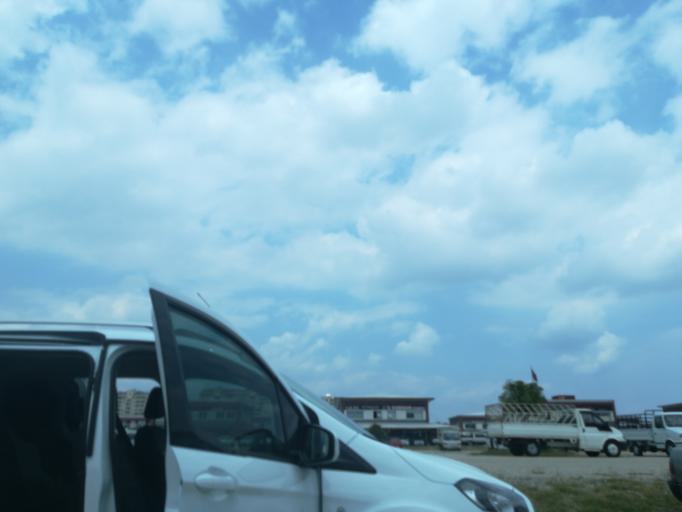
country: TR
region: Adana
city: Seyhan
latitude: 37.0003
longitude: 35.2442
